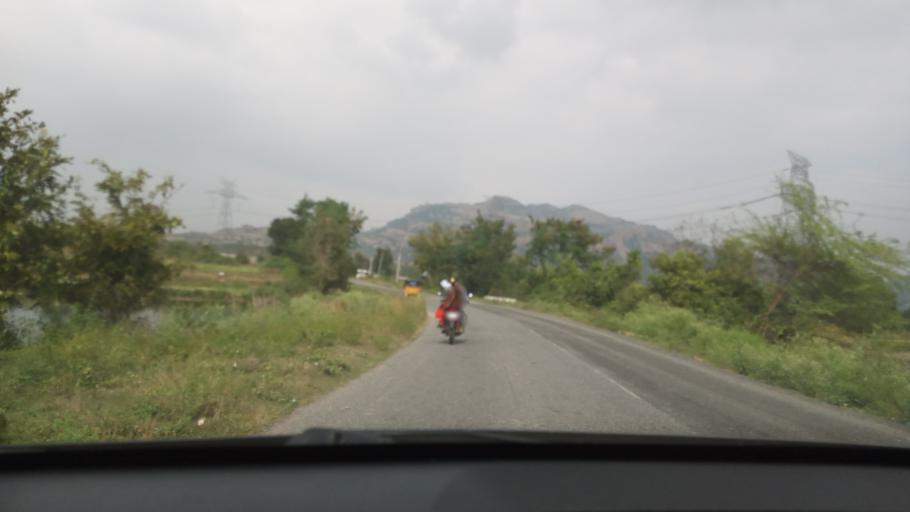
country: IN
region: Andhra Pradesh
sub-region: Chittoor
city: Madanapalle
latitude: 13.6542
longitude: 78.8354
